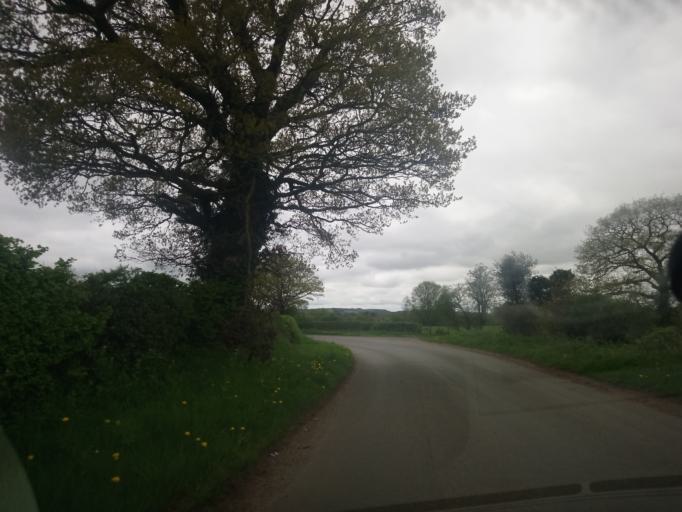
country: GB
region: England
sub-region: Shropshire
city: Stoke upon Tern
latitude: 52.8526
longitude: -2.5201
